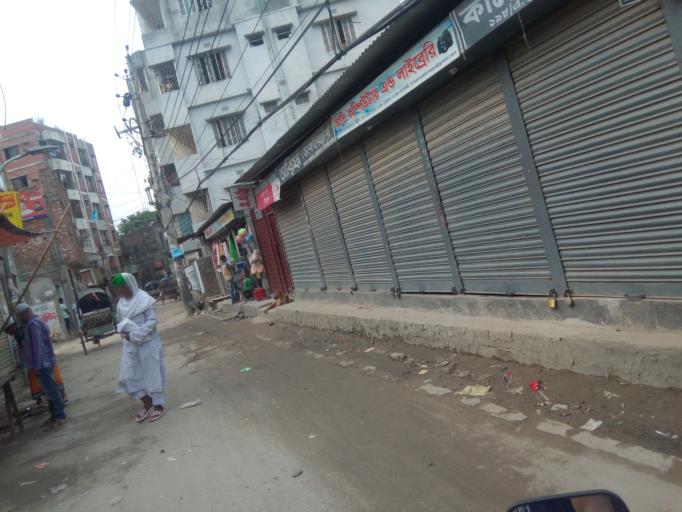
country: BD
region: Dhaka
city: Paltan
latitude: 23.7547
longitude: 90.4318
